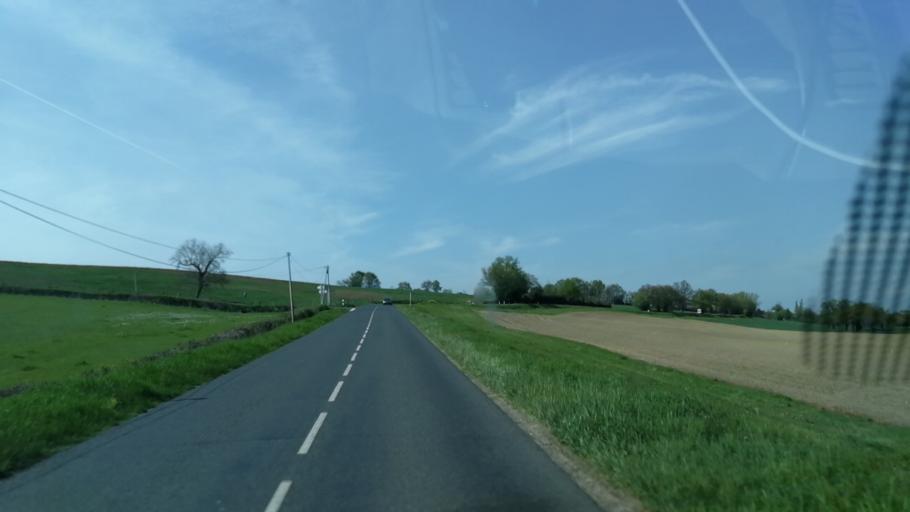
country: FR
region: Auvergne
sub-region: Departement de l'Allier
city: Saint-Gerand-le-Puy
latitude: 46.3564
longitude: 3.5776
